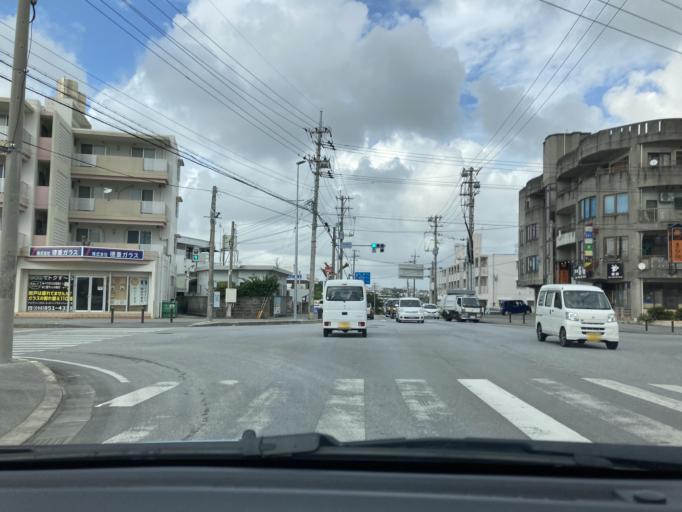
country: JP
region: Okinawa
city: Itoman
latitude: 26.1343
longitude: 127.6867
